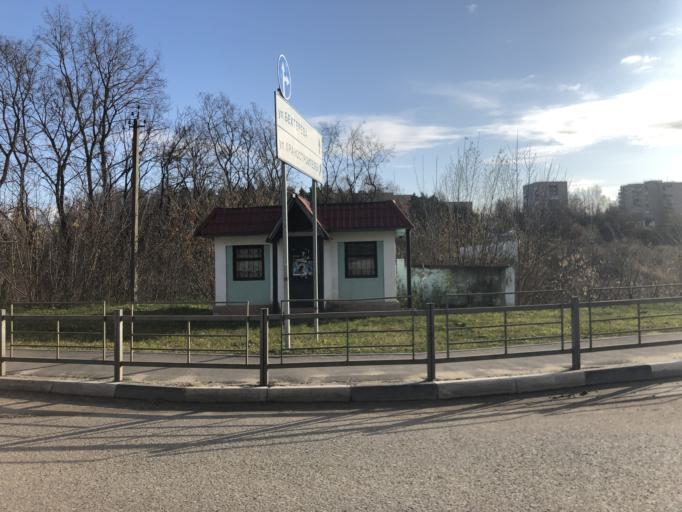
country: RU
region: Tverskaya
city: Rzhev
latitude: 56.2618
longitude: 34.3398
